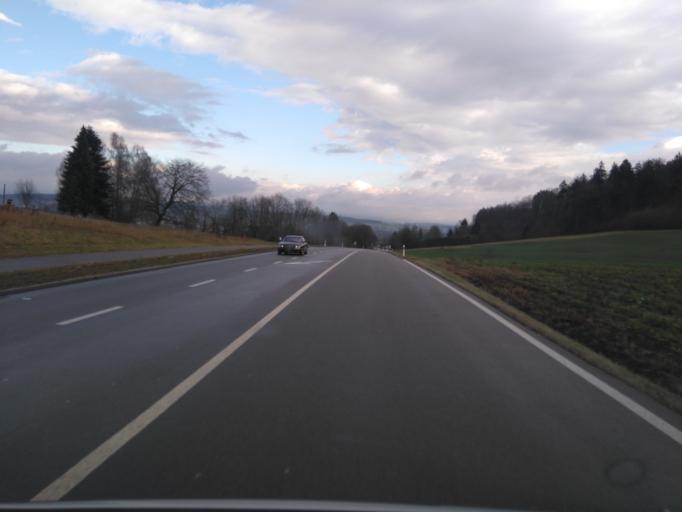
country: CH
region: Zurich
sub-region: Bezirk Dietikon
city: Unterengstringen
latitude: 47.4253
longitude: 8.4511
